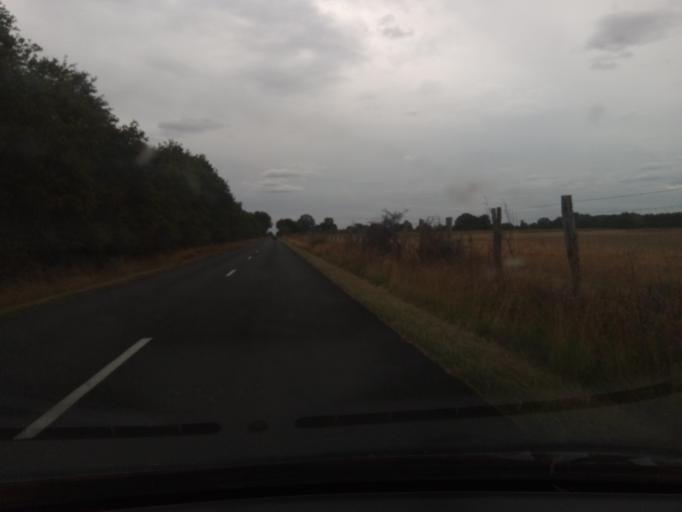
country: FR
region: Poitou-Charentes
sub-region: Departement de la Vienne
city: Pleumartin
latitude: 46.6664
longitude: 0.8050
